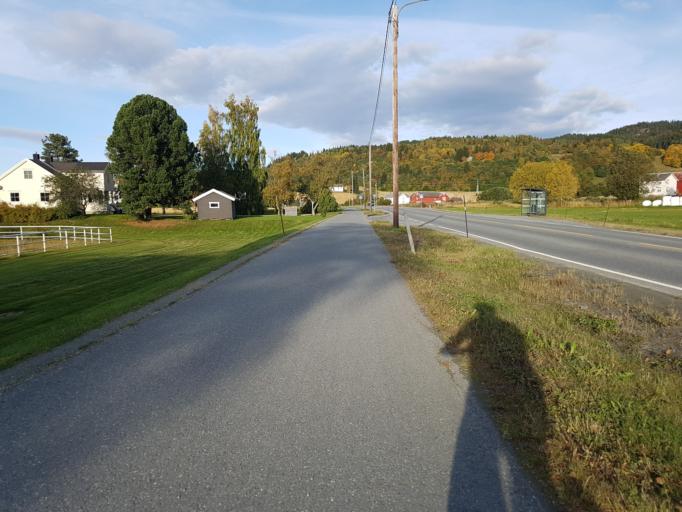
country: NO
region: Sor-Trondelag
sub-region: Trondheim
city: Trondheim
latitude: 63.3764
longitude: 10.4311
